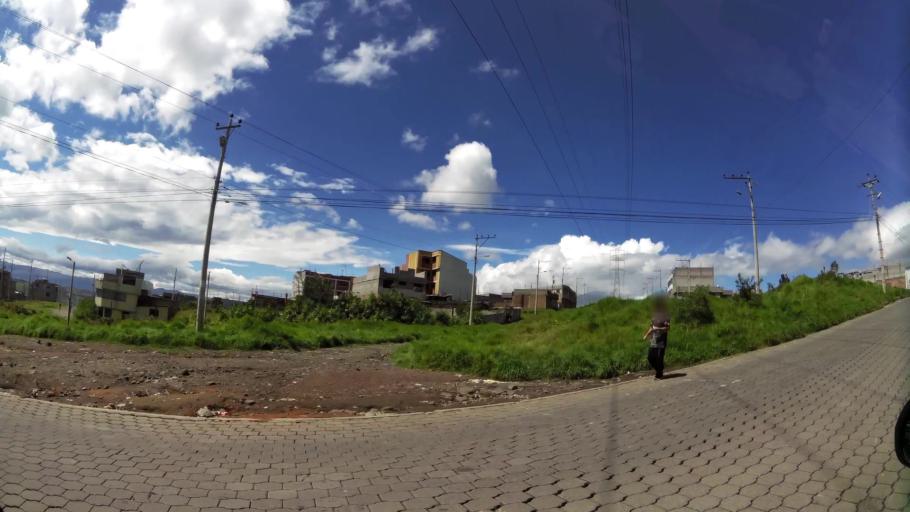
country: EC
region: Pichincha
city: Quito
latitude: -0.3289
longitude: -78.5681
